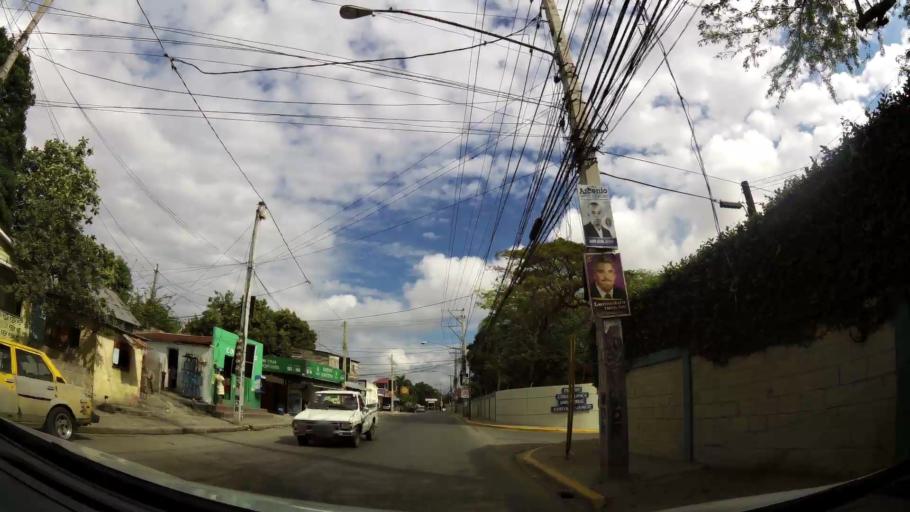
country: DO
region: Santiago
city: Santiago de los Caballeros
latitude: 19.4368
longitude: -70.7050
